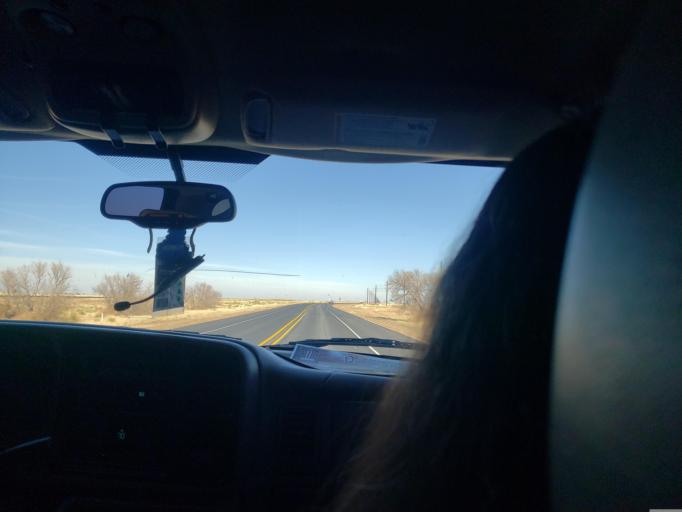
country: US
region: Texas
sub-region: Dallam County
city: Dalhart
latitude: 35.9698
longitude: -102.6412
